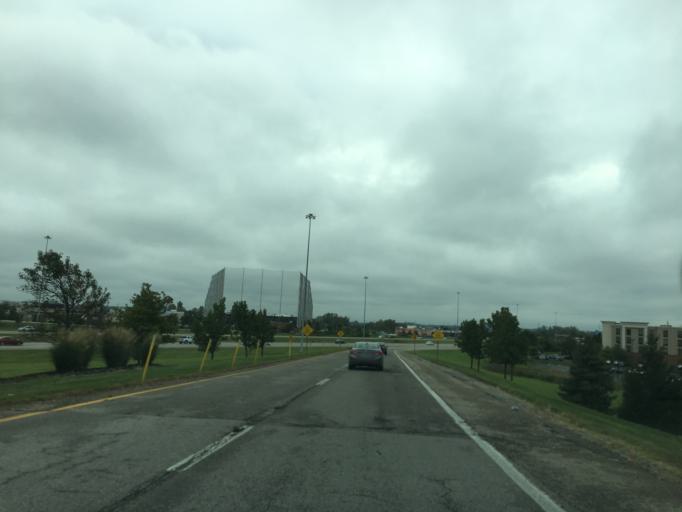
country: US
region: Ohio
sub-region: Butler County
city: Beckett Ridge
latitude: 39.3228
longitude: -84.4257
